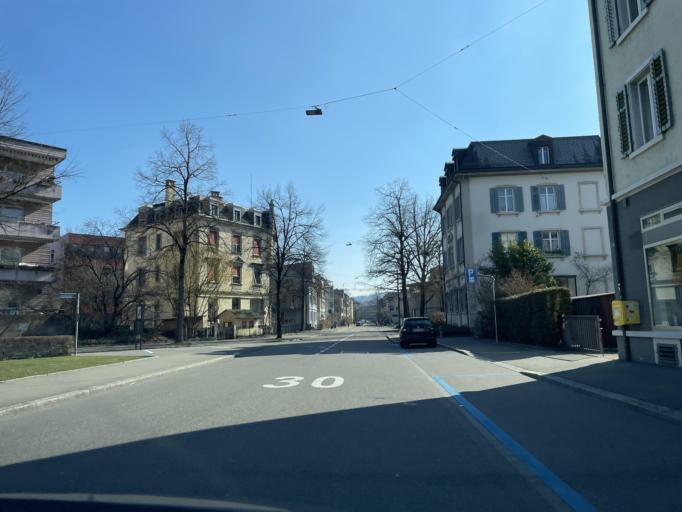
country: CH
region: Zurich
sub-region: Bezirk Winterthur
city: Veltheim (Kreis 5) / Blumenau
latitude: 47.5074
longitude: 8.7184
